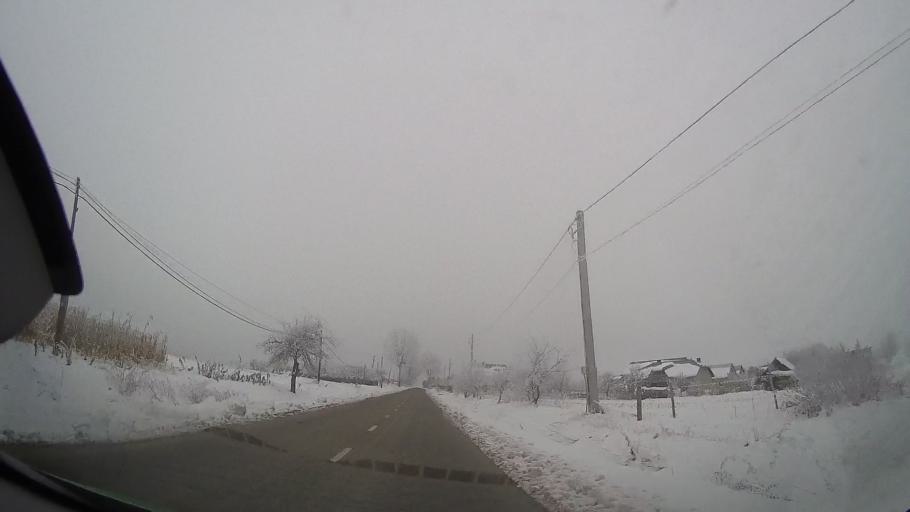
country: RO
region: Neamt
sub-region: Comuna Icusesti
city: Balusesti
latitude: 46.8656
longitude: 27.0000
